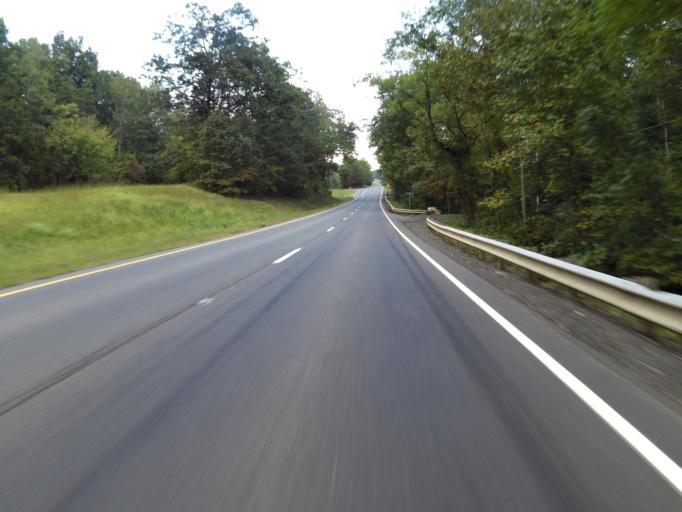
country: US
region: Virginia
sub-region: Fauquier County
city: Warrenton
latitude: 38.6737
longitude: -77.9475
